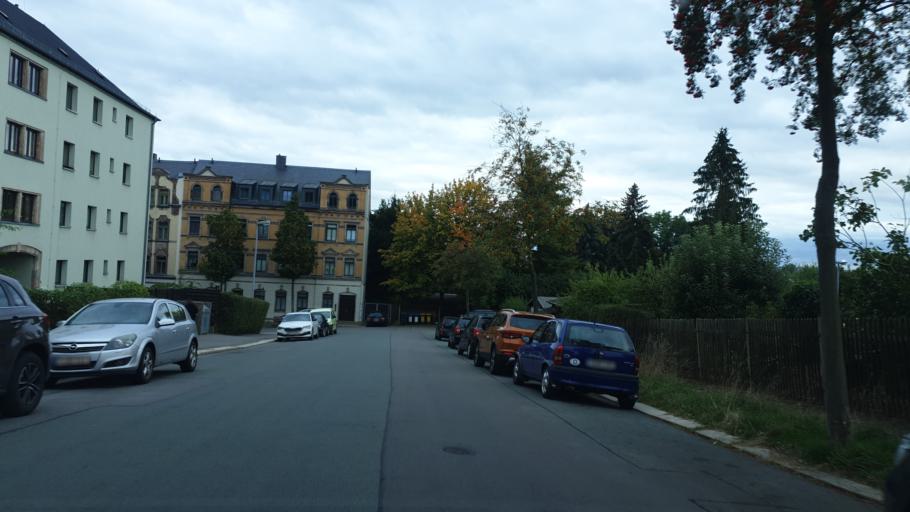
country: DE
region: Saxony
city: Chemnitz
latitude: 50.8338
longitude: 12.9463
